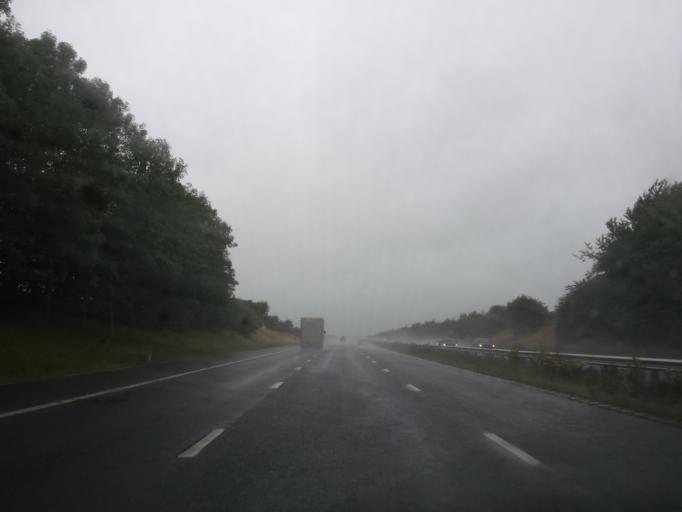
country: GB
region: England
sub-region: Leicestershire
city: Hinckley
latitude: 52.4871
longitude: -1.3912
